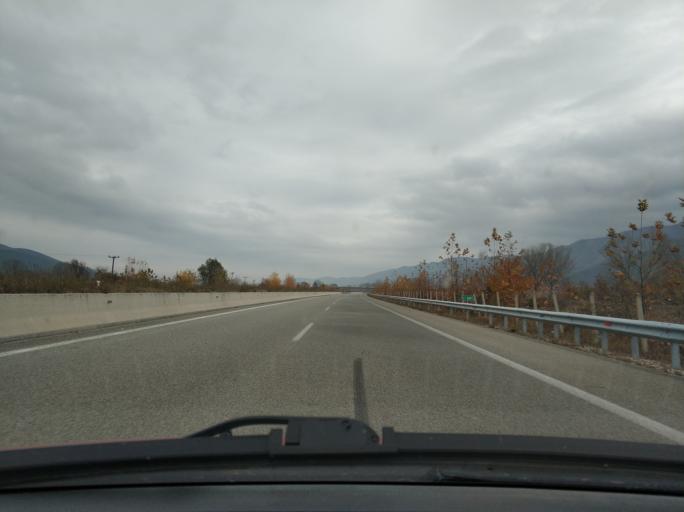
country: GR
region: East Macedonia and Thrace
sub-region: Nomos Kavalas
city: Nikisiani
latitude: 40.8500
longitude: 24.1376
